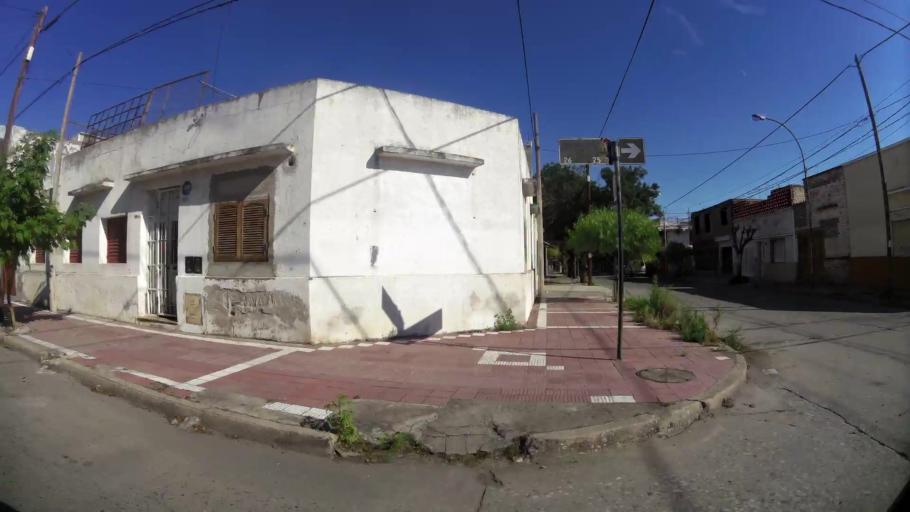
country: AR
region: Cordoba
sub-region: Departamento de Capital
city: Cordoba
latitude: -31.3953
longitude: -64.1536
